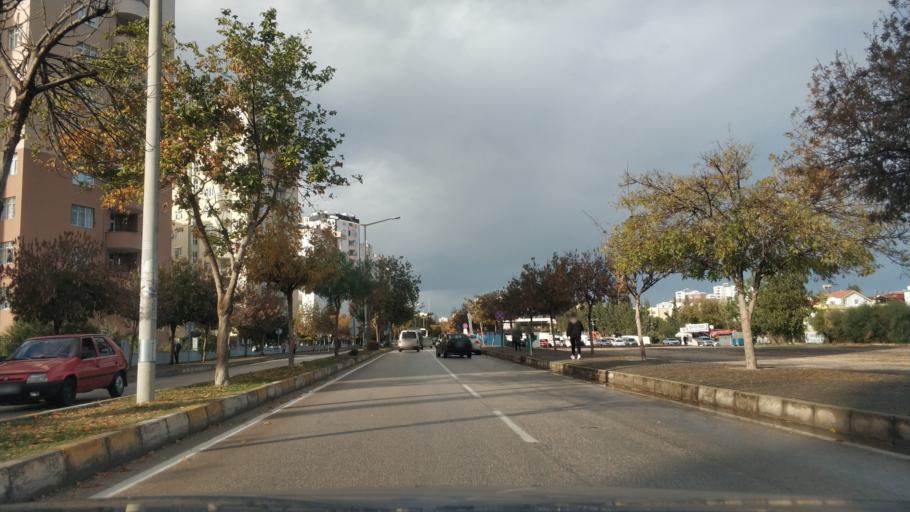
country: TR
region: Adana
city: Seyhan
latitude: 37.0392
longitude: 35.2612
